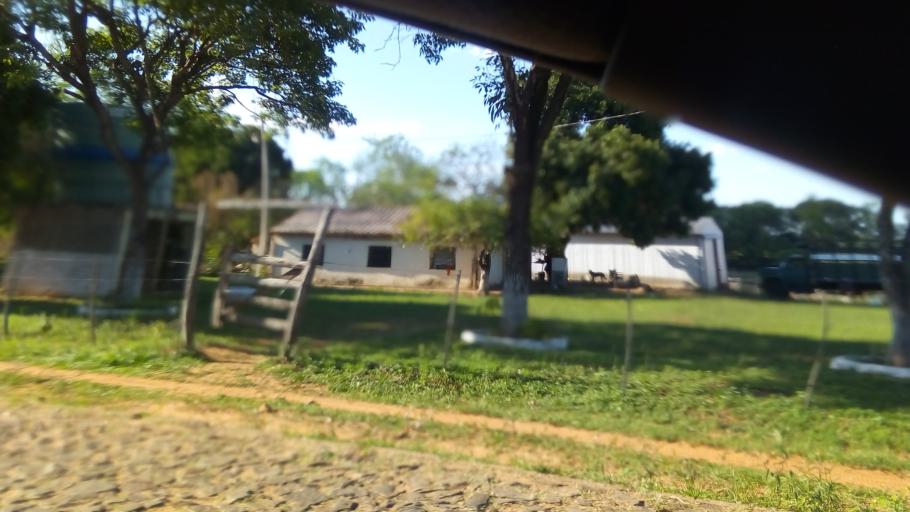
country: PY
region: Cordillera
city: Arroyos y Esteros
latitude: -24.9964
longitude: -57.1608
